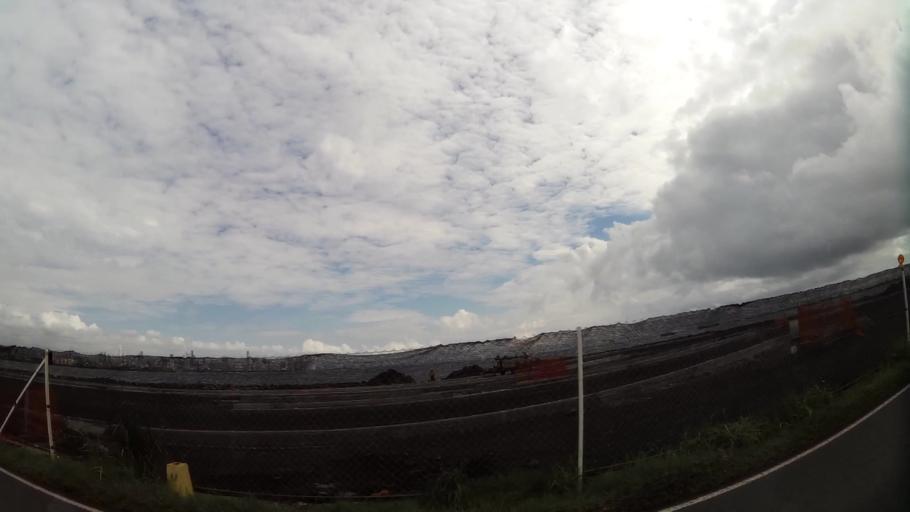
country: PA
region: Panama
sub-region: Distrito de Panama
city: Ancon
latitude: 8.9267
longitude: -79.5413
